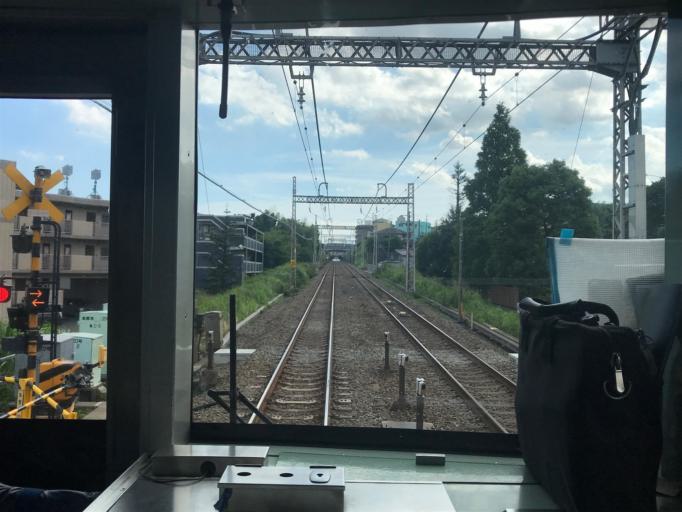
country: JP
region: Kanagawa
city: Atsugi
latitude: 35.4214
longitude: 139.3488
